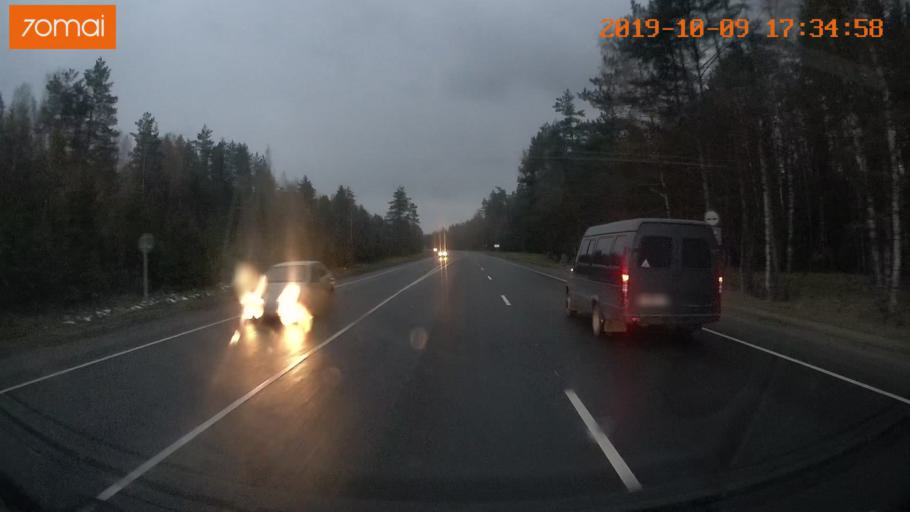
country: RU
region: Ivanovo
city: Bogorodskoye
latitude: 57.1007
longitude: 41.0065
